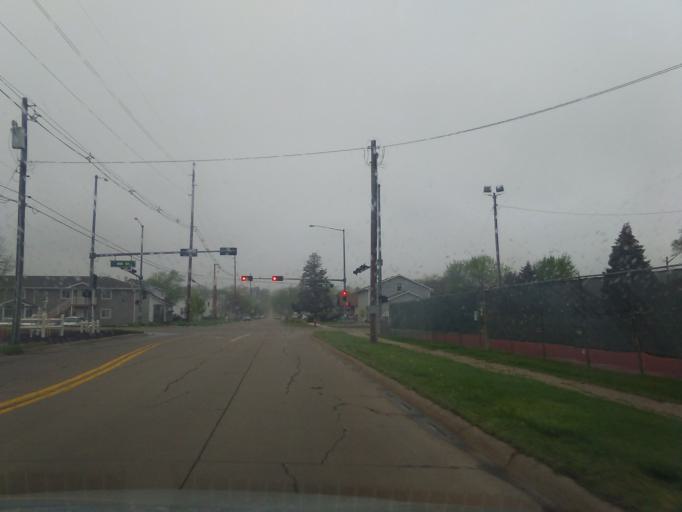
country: US
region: Nebraska
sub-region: Madison County
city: Norfolk
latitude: 42.0383
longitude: -97.4112
